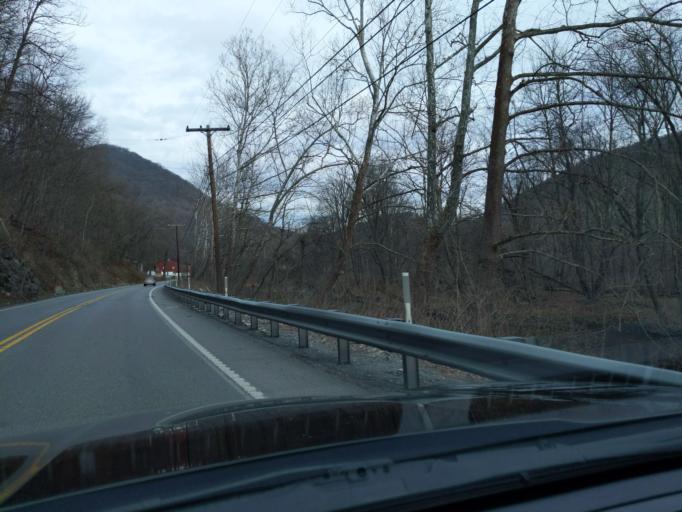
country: US
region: Pennsylvania
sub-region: Blair County
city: Williamsburg
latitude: 40.4798
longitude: -78.2619
